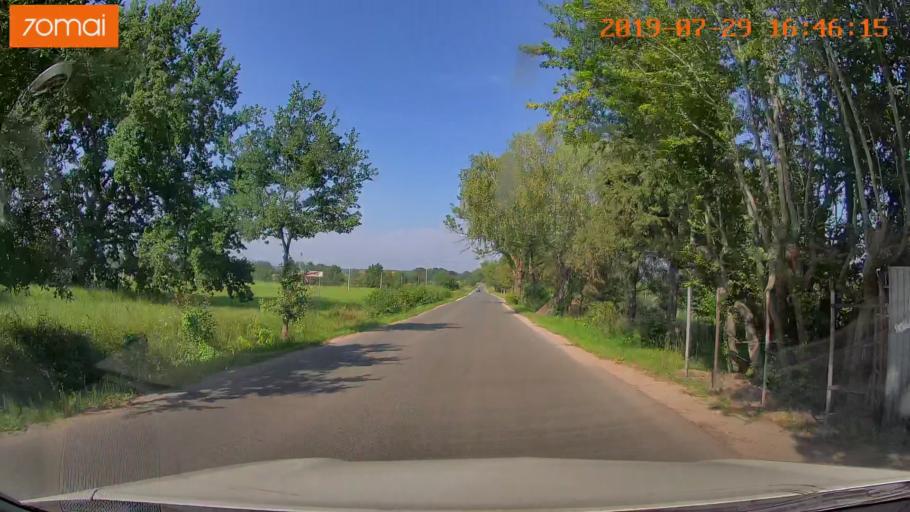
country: RU
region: Kaliningrad
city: Primorsk
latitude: 54.7723
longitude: 20.0826
